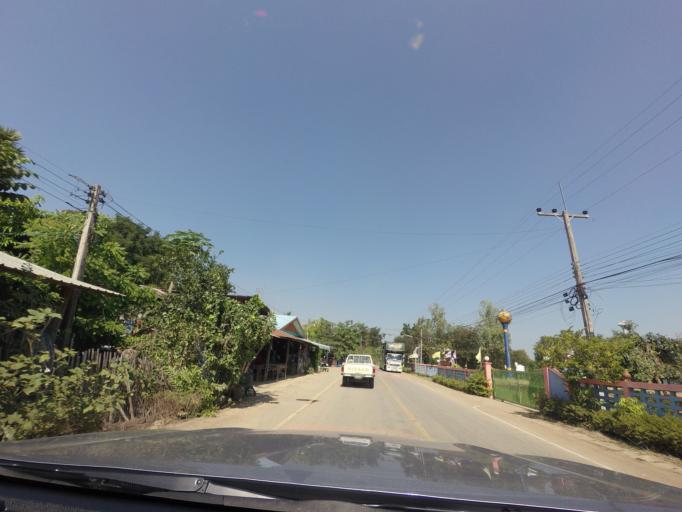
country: TH
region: Sukhothai
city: Si Samrong
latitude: 17.1693
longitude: 99.7699
